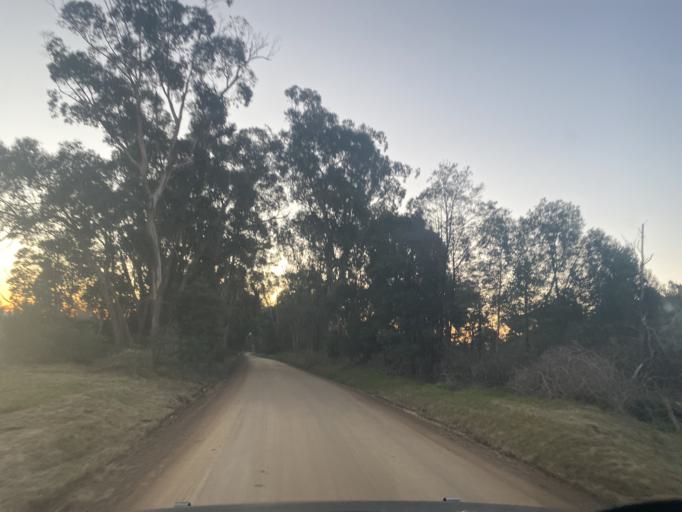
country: AU
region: Victoria
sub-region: Murrindindi
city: Kinglake West
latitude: -37.4189
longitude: 145.4672
